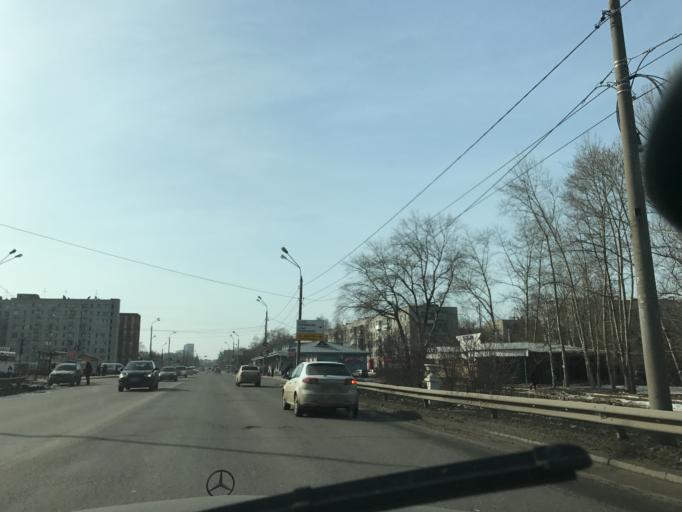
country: RU
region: Nizjnij Novgorod
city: Gorbatovka
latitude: 56.2674
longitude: 43.8784
